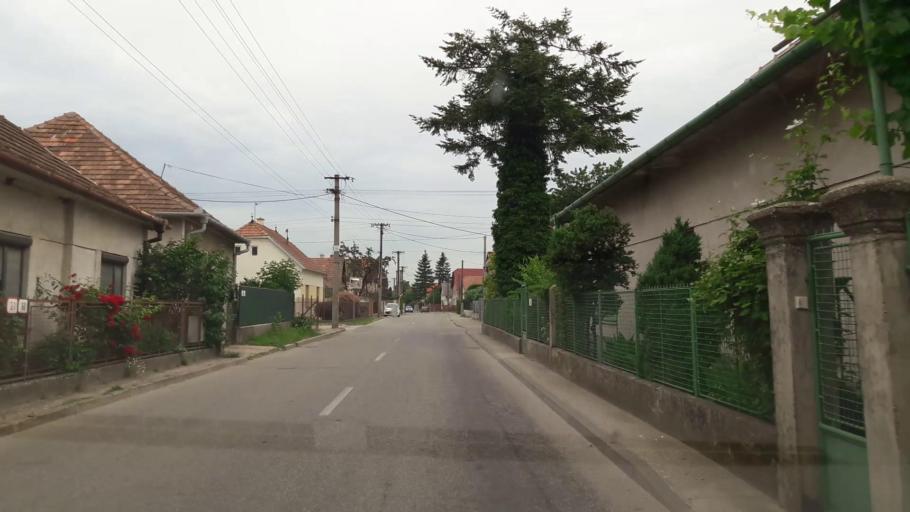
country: SK
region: Bratislavsky
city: Senec
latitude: 48.2088
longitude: 17.3612
